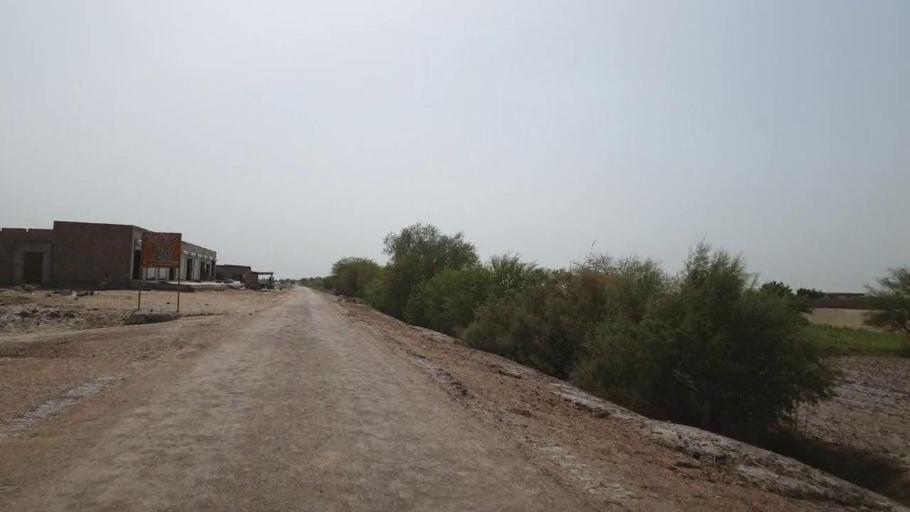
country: PK
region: Sindh
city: Bandhi
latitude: 26.5386
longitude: 68.3965
